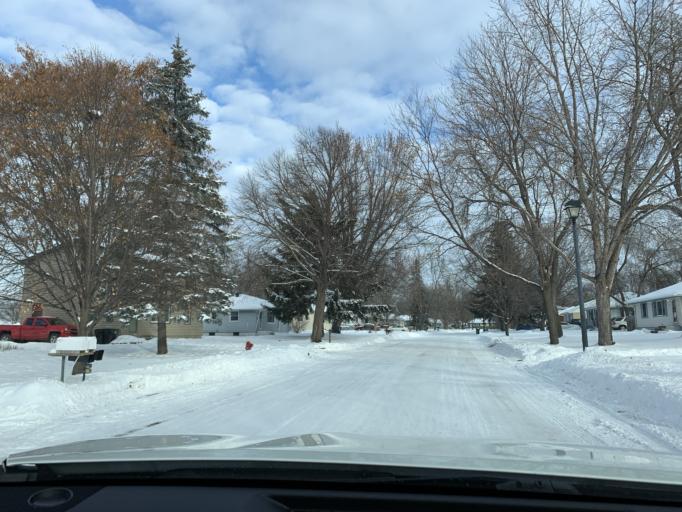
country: US
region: Minnesota
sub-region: Anoka County
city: Blaine
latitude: 45.1766
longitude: -93.2879
